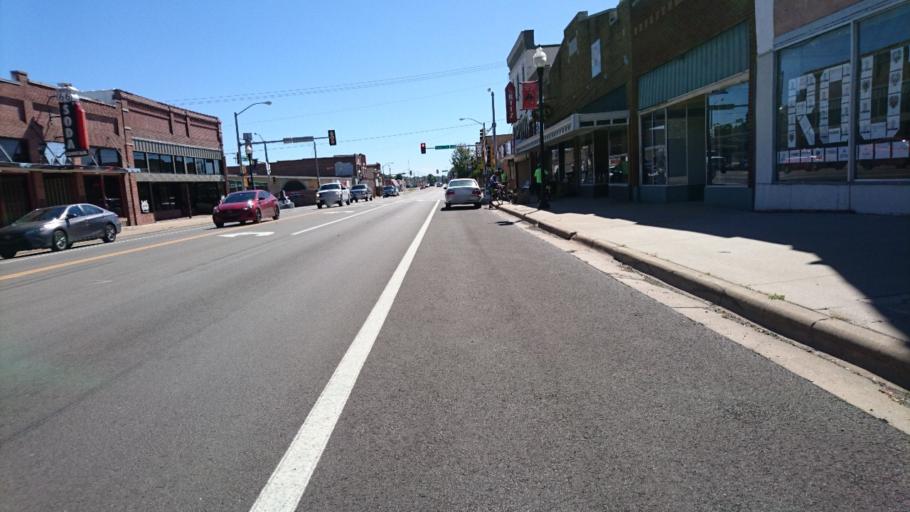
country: US
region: Kansas
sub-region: Cherokee County
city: Baxter Springs
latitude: 37.0243
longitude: -94.7353
